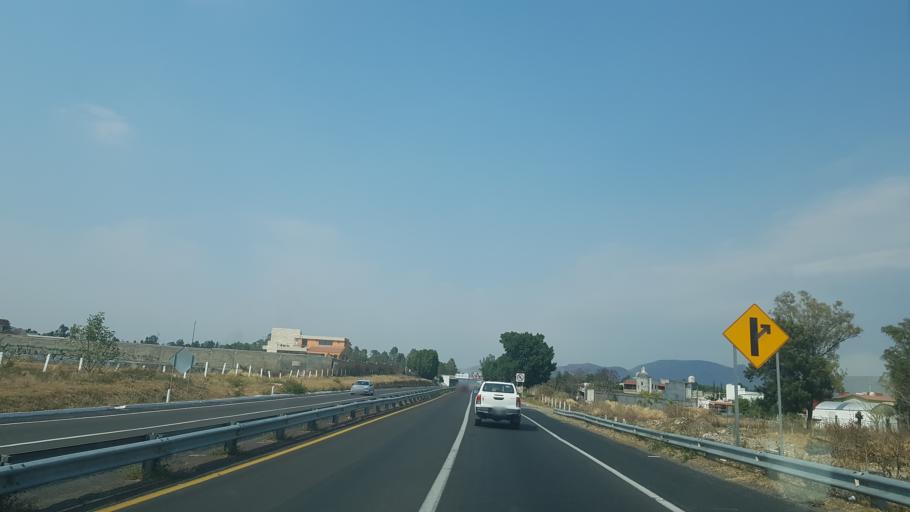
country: MX
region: Puebla
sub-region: Atlixco
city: San Agustin Huixaxtla
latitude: 18.9250
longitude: -98.4003
